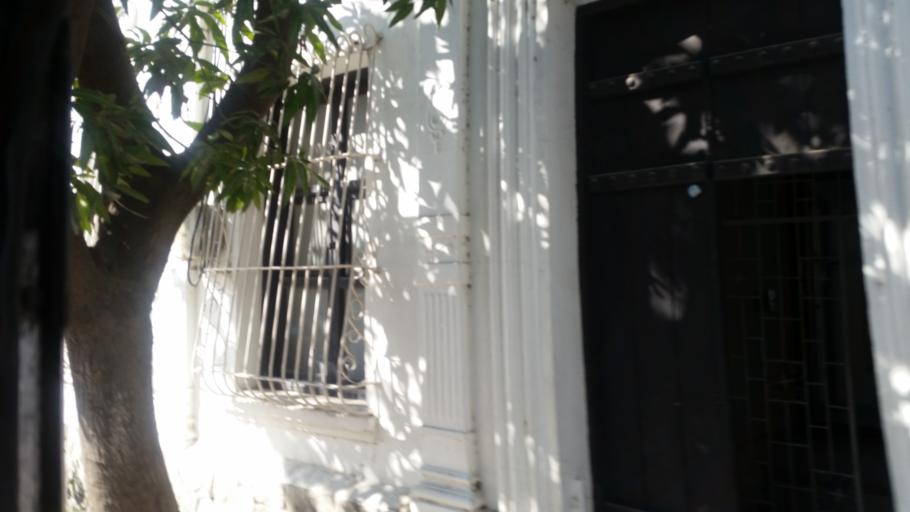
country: CO
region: Magdalena
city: Santa Marta
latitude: 11.2472
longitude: -74.2132
